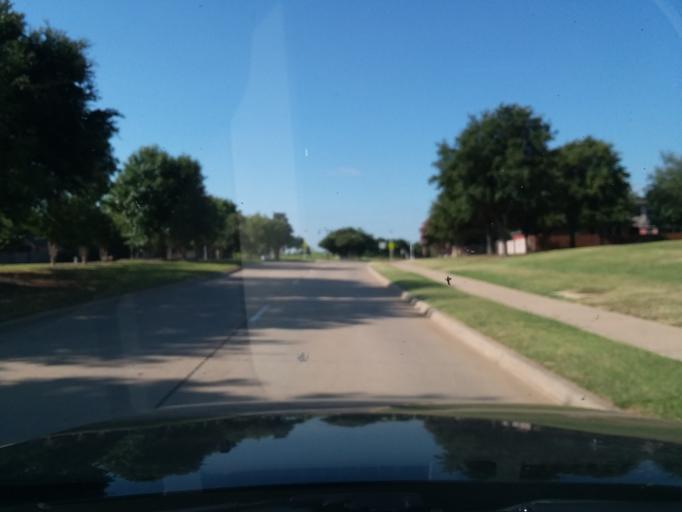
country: US
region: Texas
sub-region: Denton County
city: Double Oak
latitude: 33.0605
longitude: -97.0942
